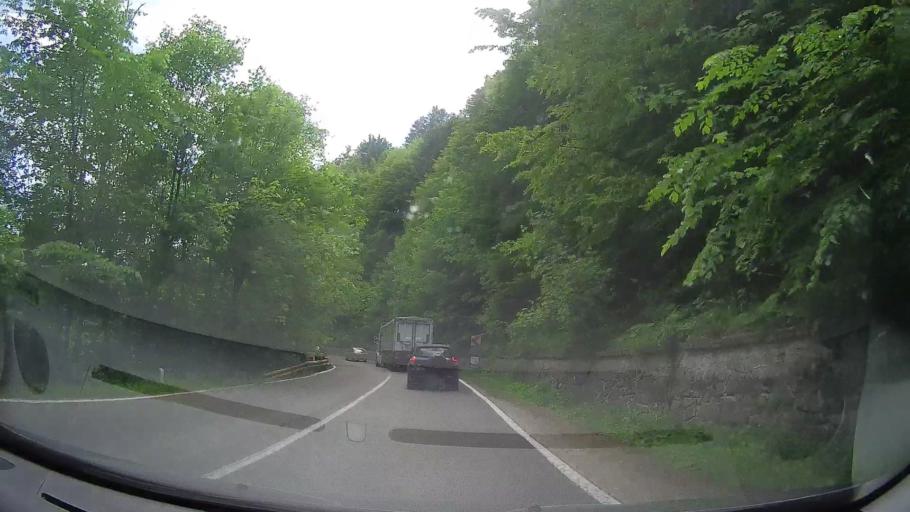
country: RO
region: Prahova
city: Maneciu
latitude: 45.3690
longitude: 25.9294
